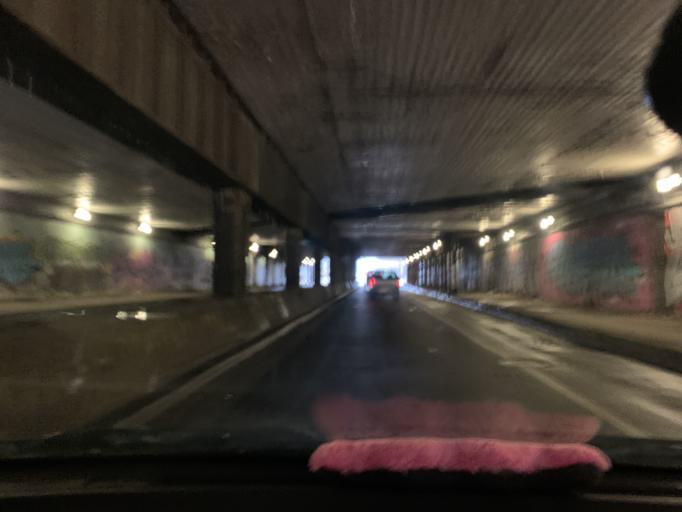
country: US
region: Illinois
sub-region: Cook County
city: Chicago
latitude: 41.8620
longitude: -87.6761
